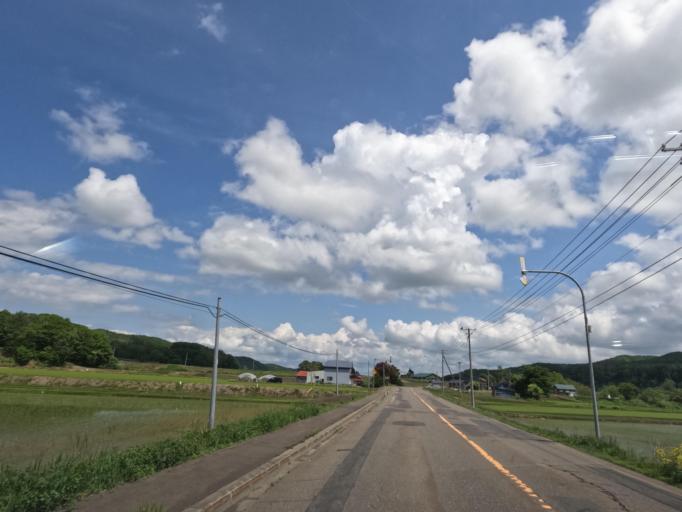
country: JP
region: Hokkaido
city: Takikawa
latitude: 43.5857
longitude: 141.7847
